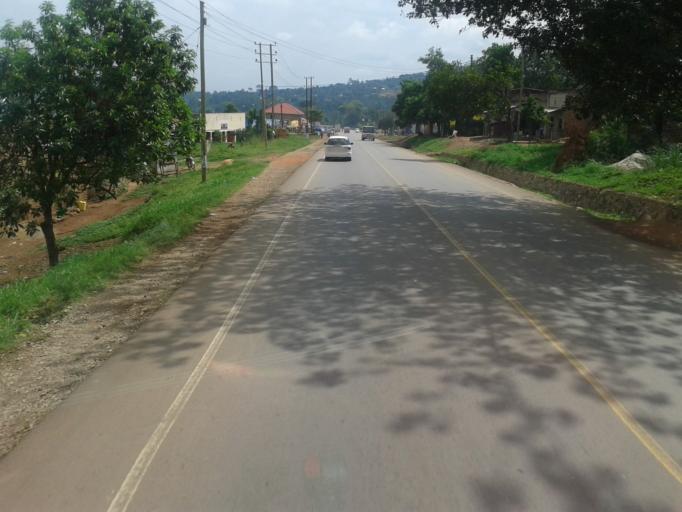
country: UG
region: Central Region
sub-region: Wakiso District
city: Wakiso
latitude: 0.5040
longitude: 32.5234
